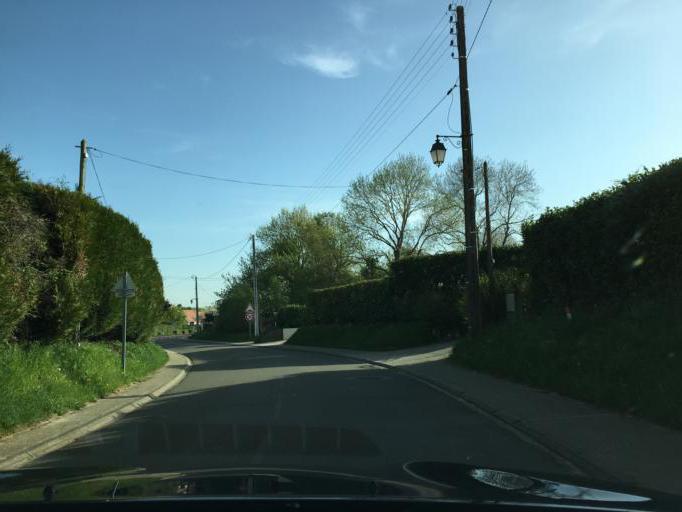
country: FR
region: Ile-de-France
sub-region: Departement des Yvelines
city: Conde-sur-Vesgre
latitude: 48.7255
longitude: 1.6557
